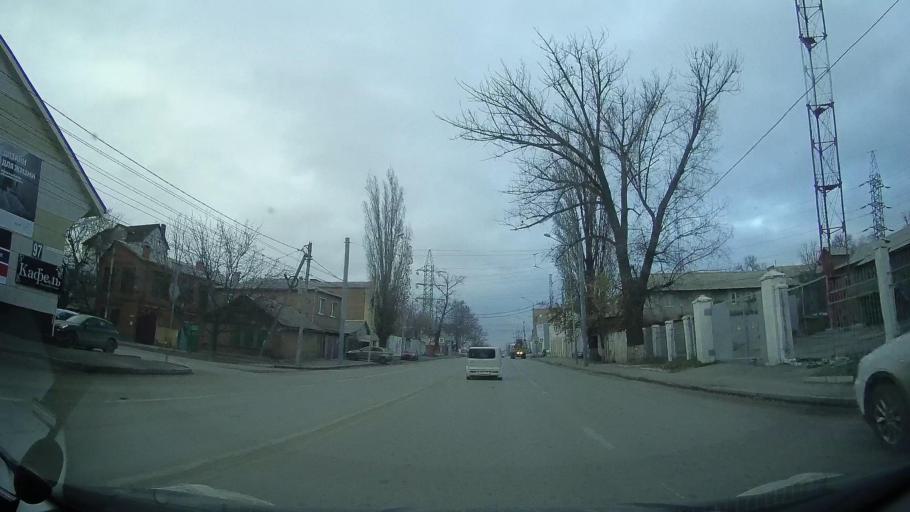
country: RU
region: Rostov
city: Rostov-na-Donu
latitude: 47.2374
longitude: 39.7370
